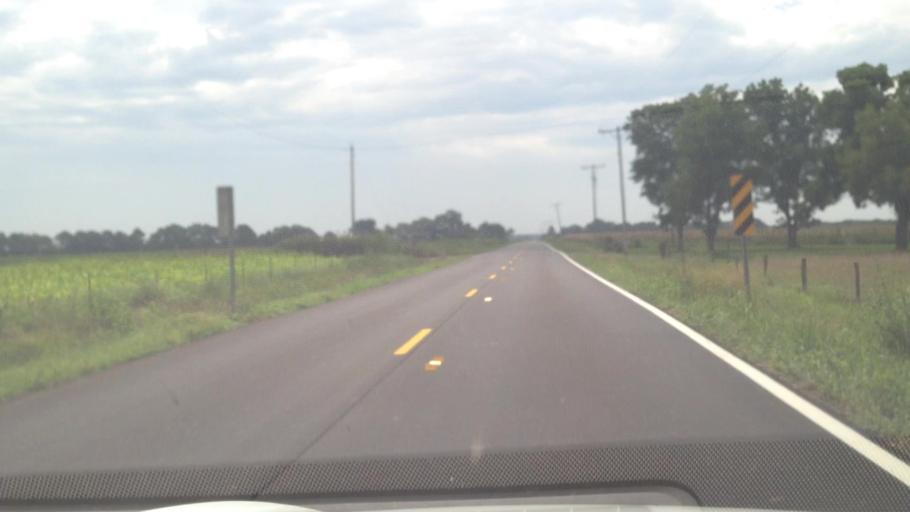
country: US
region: Kansas
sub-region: Crawford County
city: Girard
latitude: 37.6299
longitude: -94.9698
